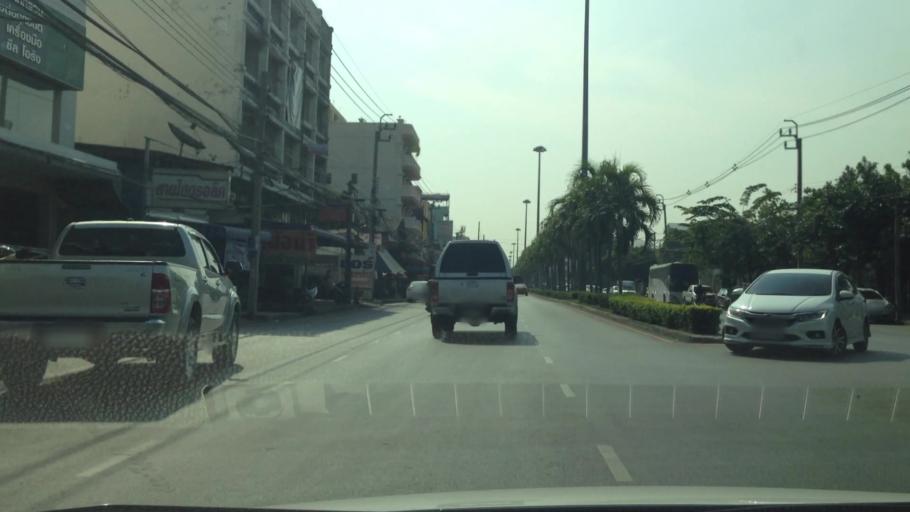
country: TH
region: Samut Prakan
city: Samut Prakan
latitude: 13.5868
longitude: 100.5989
